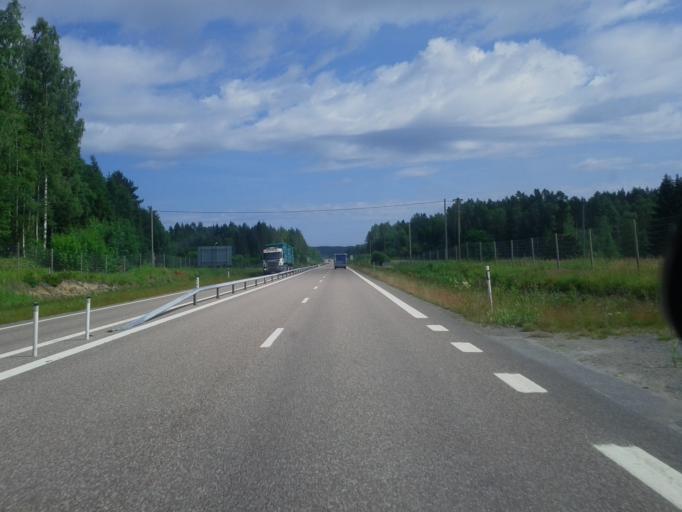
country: SE
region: Vaesternorrland
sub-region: OErnskoeldsviks Kommun
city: Husum
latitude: 63.3195
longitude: 19.0248
